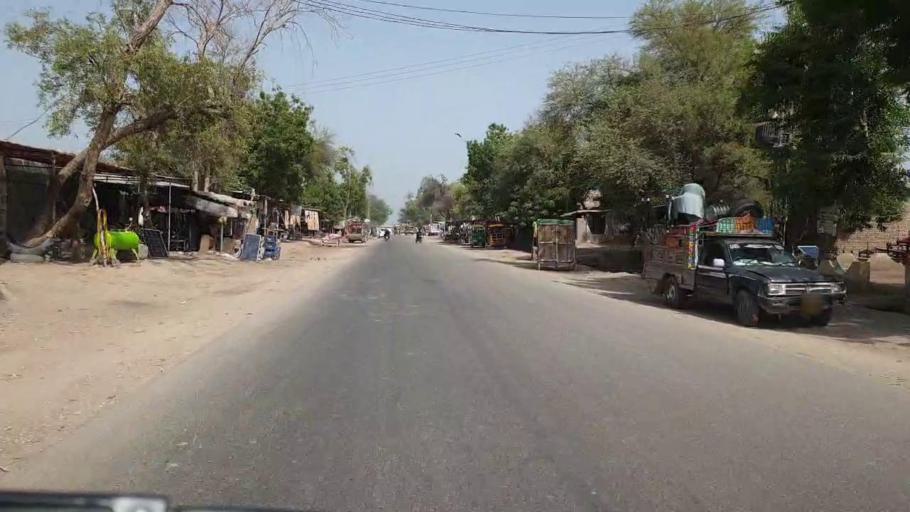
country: PK
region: Sindh
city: Sakrand
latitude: 26.2745
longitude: 68.1533
